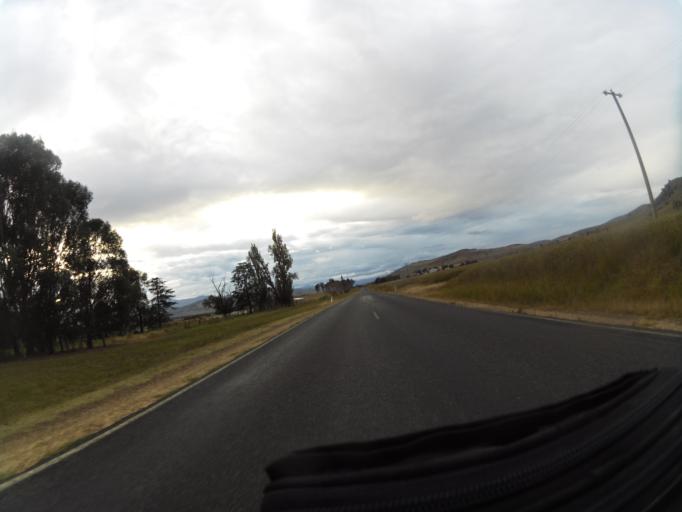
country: AU
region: New South Wales
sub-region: Greater Hume Shire
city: Holbrook
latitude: -36.0551
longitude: 147.9388
